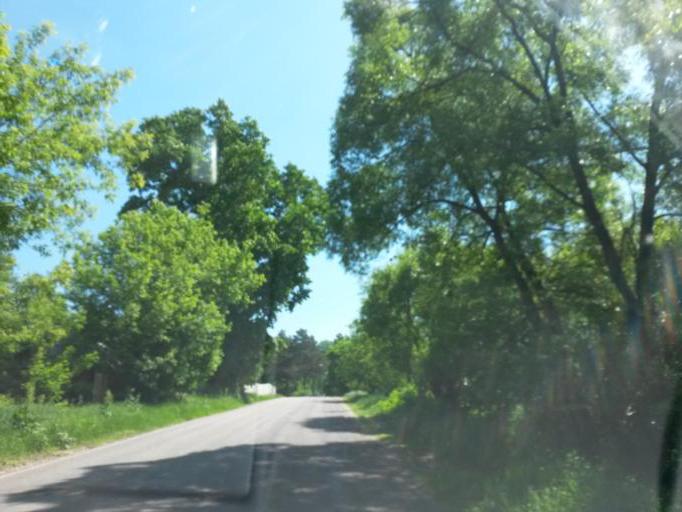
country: RU
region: Moskovskaya
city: Danki
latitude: 54.9132
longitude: 37.5693
